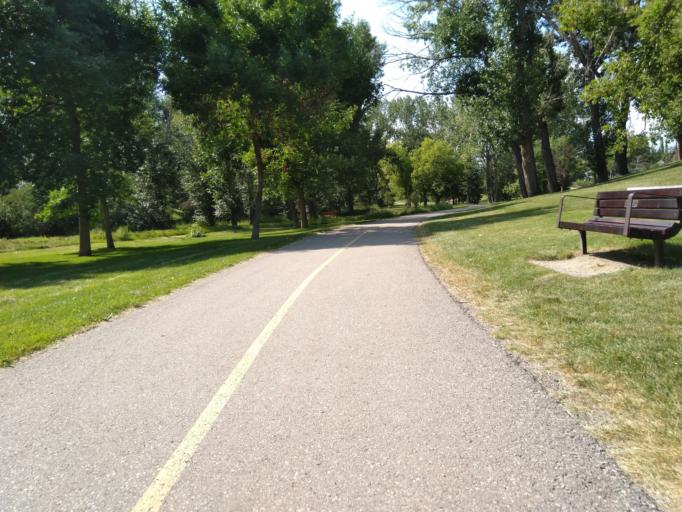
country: CA
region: Alberta
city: Calgary
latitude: 51.0736
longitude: -114.0910
